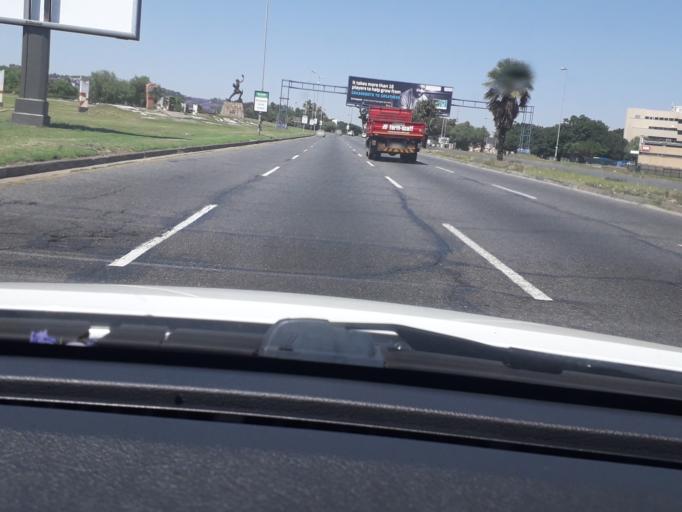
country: ZA
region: Gauteng
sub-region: City of Johannesburg Metropolitan Municipality
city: Johannesburg
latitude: -26.1798
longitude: 28.1138
